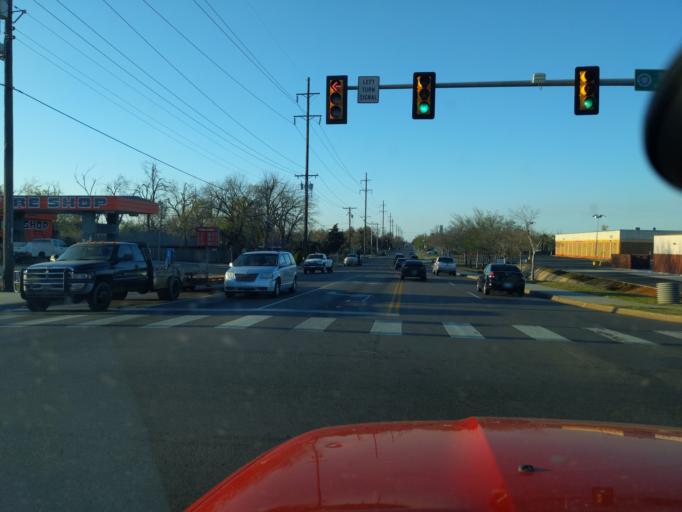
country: US
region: Oklahoma
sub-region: Oklahoma County
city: Oklahoma City
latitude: 35.4063
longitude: -97.5213
